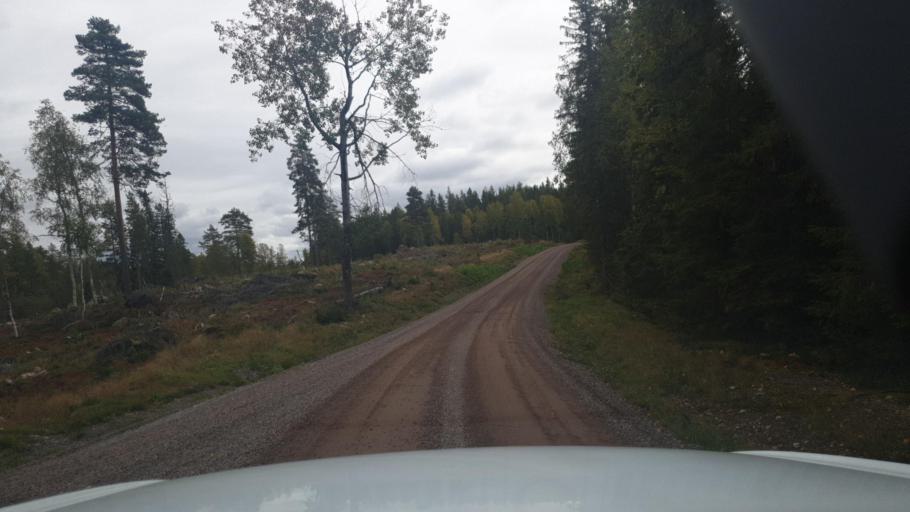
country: SE
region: Vaermland
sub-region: Eda Kommun
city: Charlottenberg
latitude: 60.0468
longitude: 12.5736
